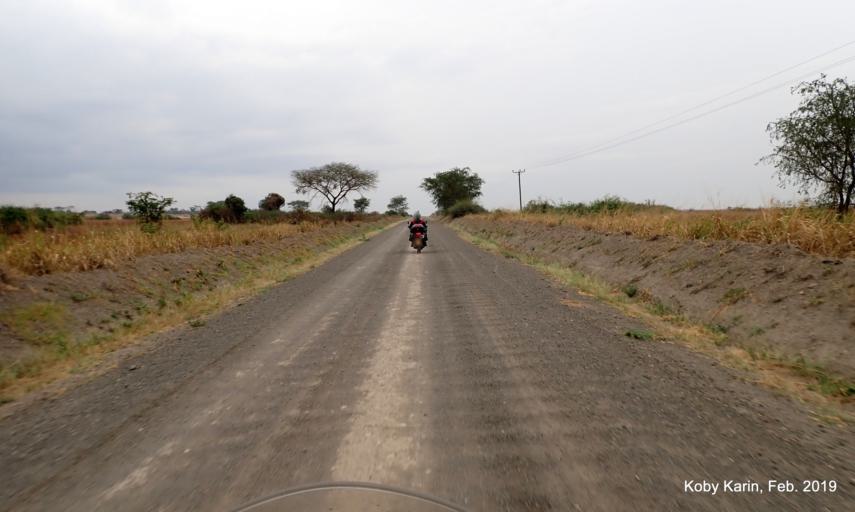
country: UG
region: Western Region
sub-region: Rubirizi District
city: Rubirizi
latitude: -0.0987
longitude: 29.9637
